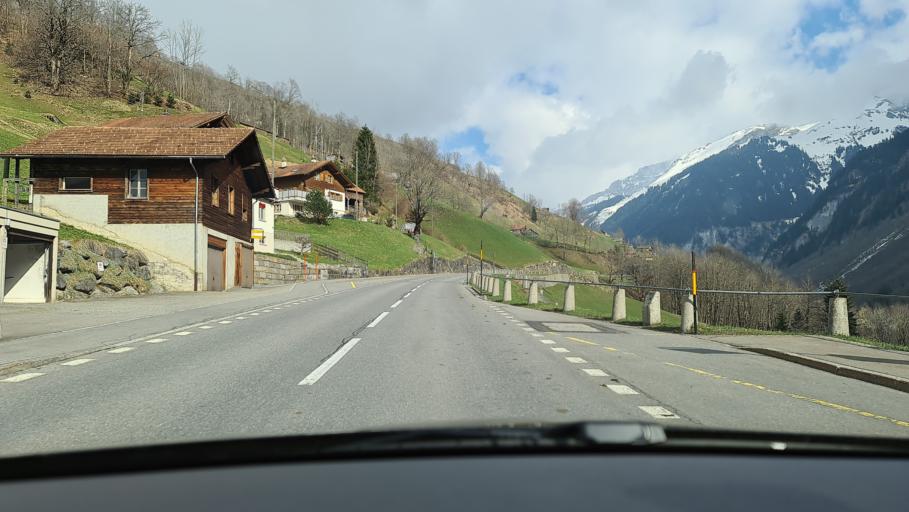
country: CH
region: Uri
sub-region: Uri
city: Burglen
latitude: 46.8710
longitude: 8.7401
